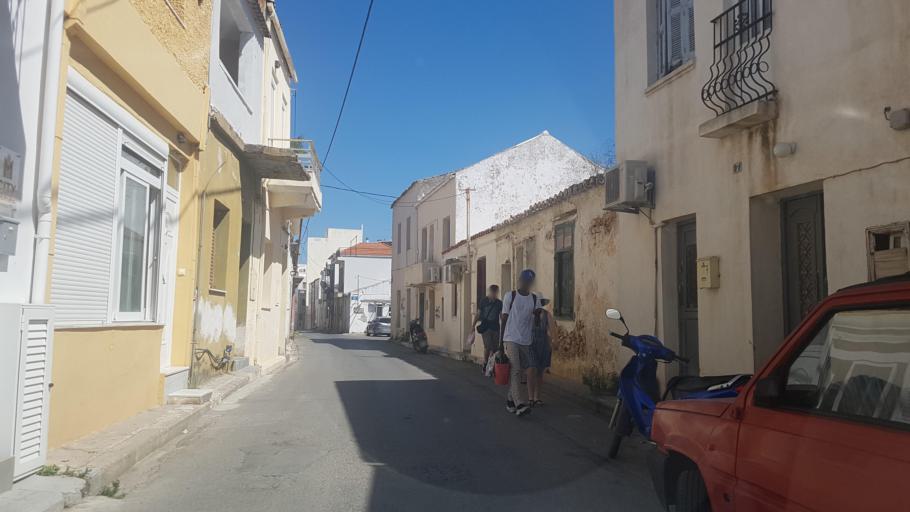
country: GR
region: Crete
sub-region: Nomos Chanias
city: Chania
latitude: 35.5140
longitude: 24.0105
